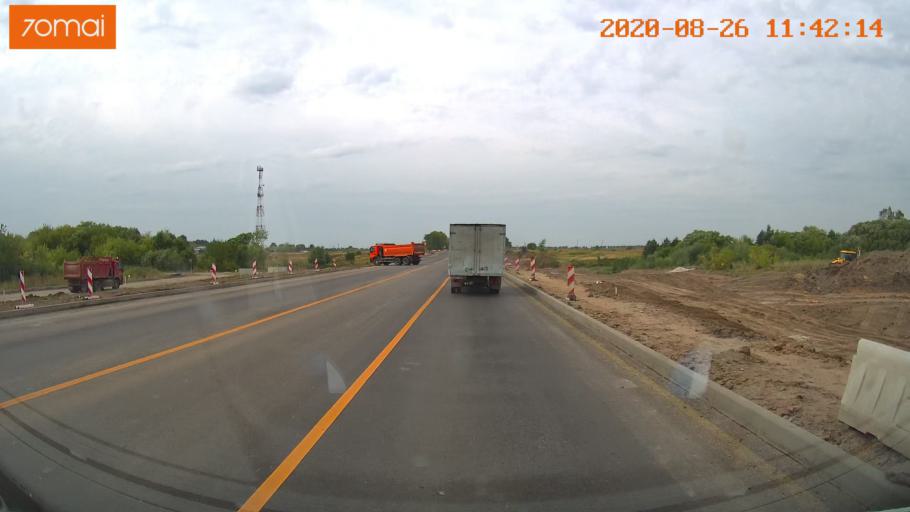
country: RU
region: Rjazan
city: Shilovo
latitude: 54.2971
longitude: 40.6975
